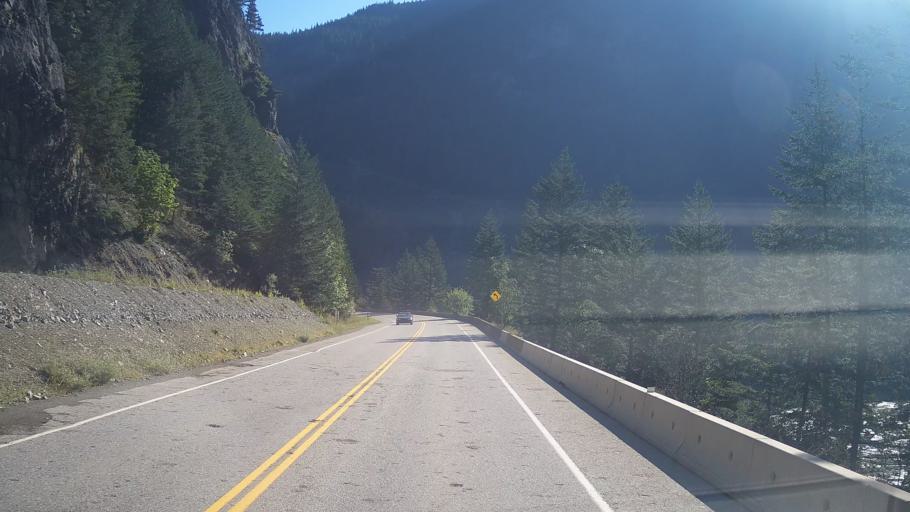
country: CA
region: British Columbia
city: Hope
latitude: 49.5635
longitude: -121.4034
